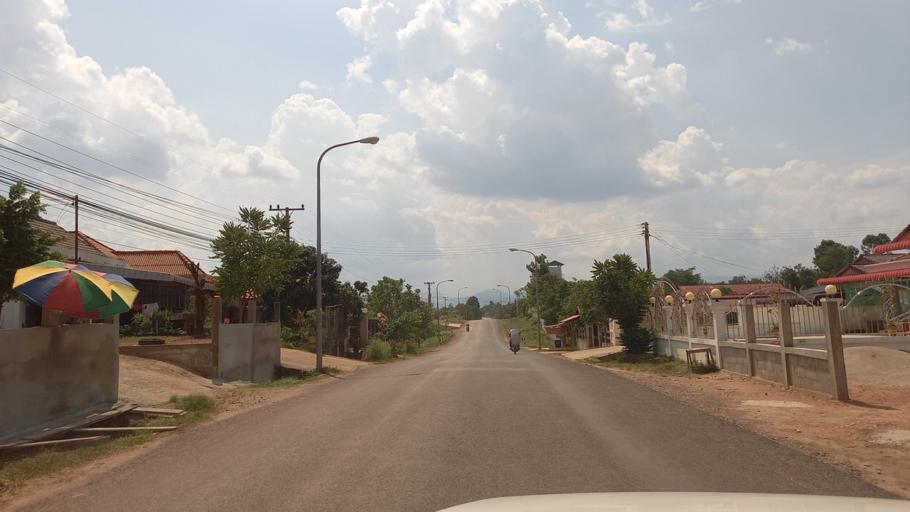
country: LA
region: Bolikhamxai
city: Muang Pakxan
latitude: 18.4180
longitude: 103.6370
